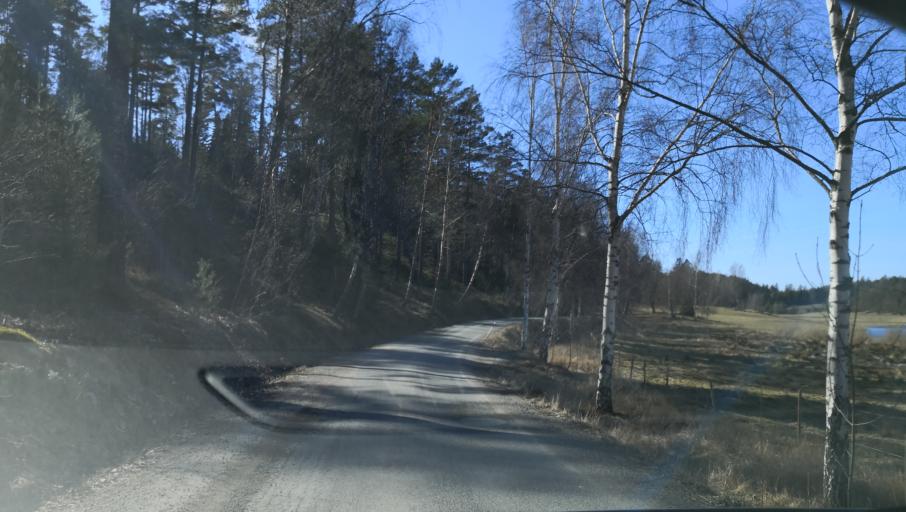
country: SE
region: Stockholm
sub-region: Varmdo Kommun
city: Gustavsberg
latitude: 59.2970
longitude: 18.4040
